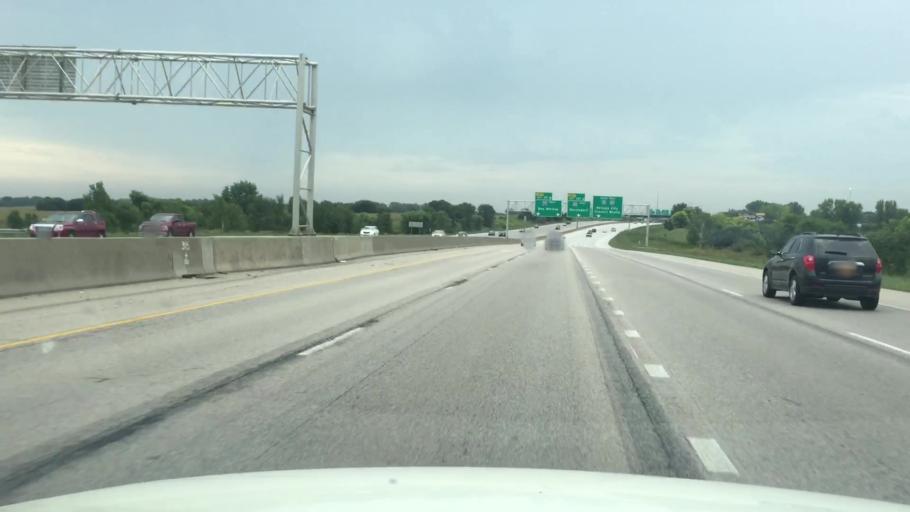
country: US
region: Iowa
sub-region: Polk County
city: Saylorville
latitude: 41.6671
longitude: -93.5770
